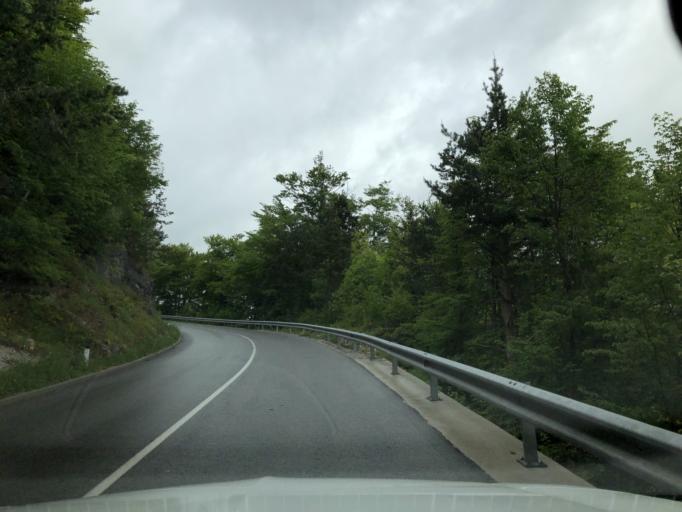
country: SI
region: Jesenice
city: Slovenski Javornik
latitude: 46.4183
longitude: 14.0866
